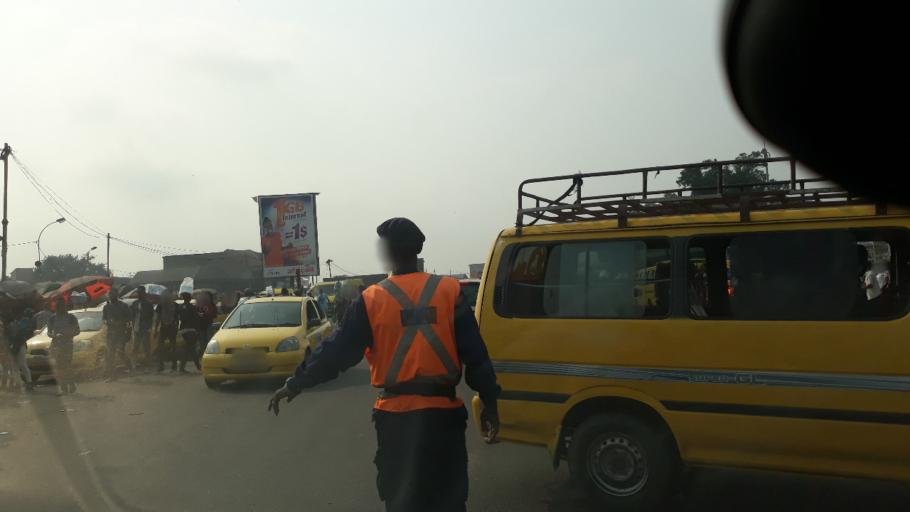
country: CD
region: Kinshasa
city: Kinshasa
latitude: -4.4072
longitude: 15.2564
